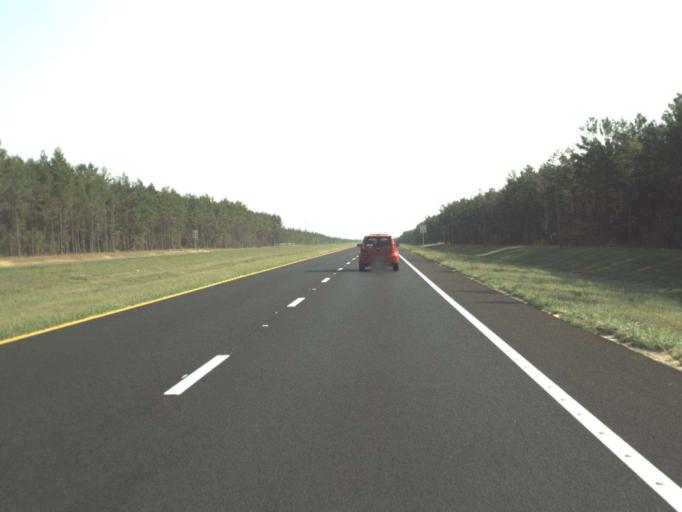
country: US
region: Florida
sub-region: Holmes County
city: Bonifay
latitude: 30.5481
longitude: -85.8261
